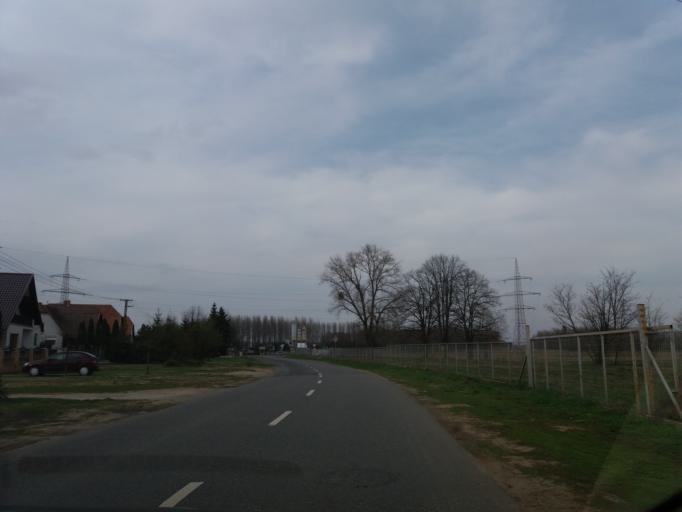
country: HU
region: Szabolcs-Szatmar-Bereg
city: Anarcs
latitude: 48.1854
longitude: 22.1020
